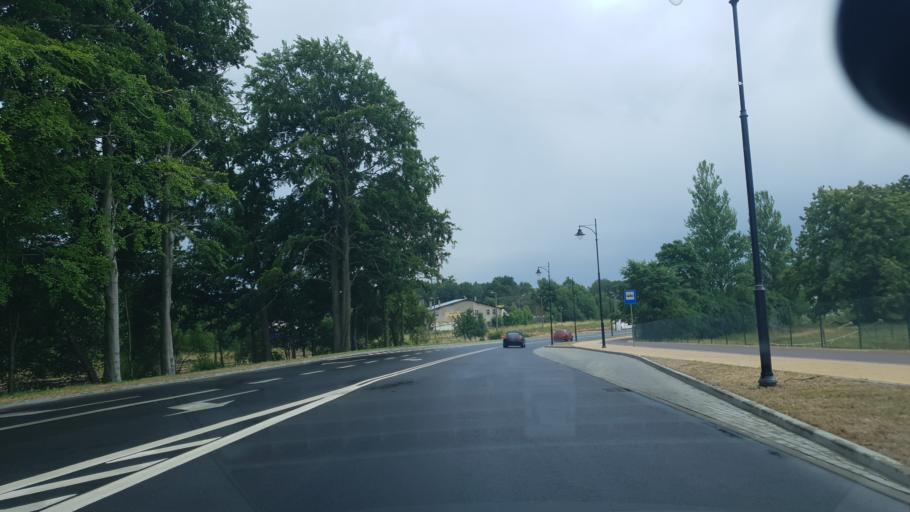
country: PL
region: Pomeranian Voivodeship
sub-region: Powiat kartuski
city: Kartuzy
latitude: 54.3383
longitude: 18.2070
